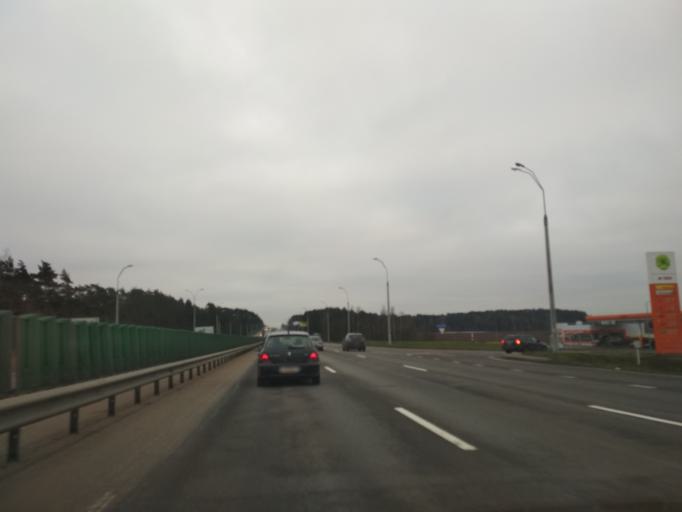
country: BY
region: Minsk
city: Vyaliki Trastsyanets
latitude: 53.8339
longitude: 27.7349
